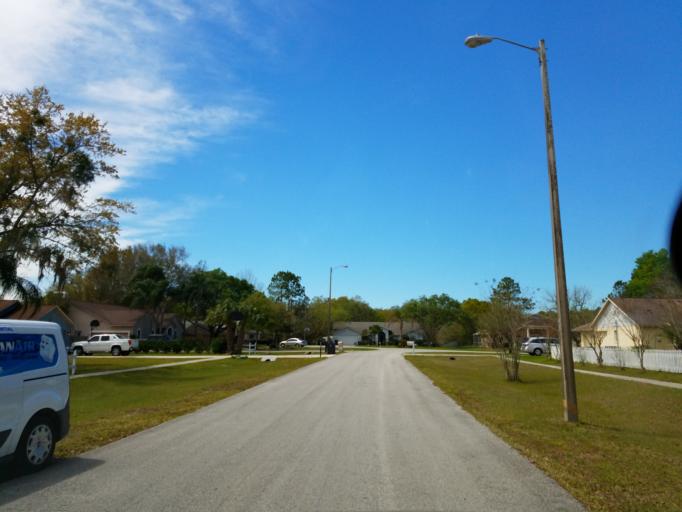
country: US
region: Florida
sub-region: Hillsborough County
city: Thonotosassa
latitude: 28.0655
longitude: -82.3095
